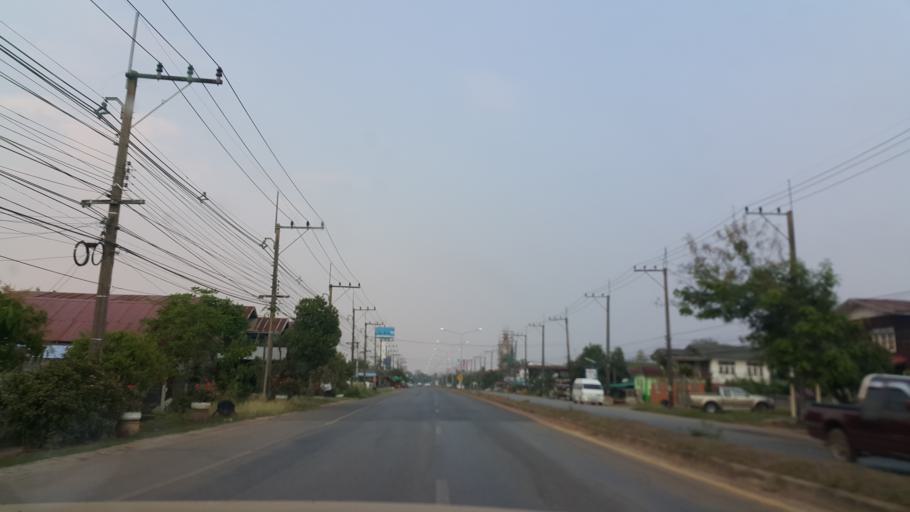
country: TH
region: Nakhon Phanom
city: That Phanom
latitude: 16.9776
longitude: 104.7274
